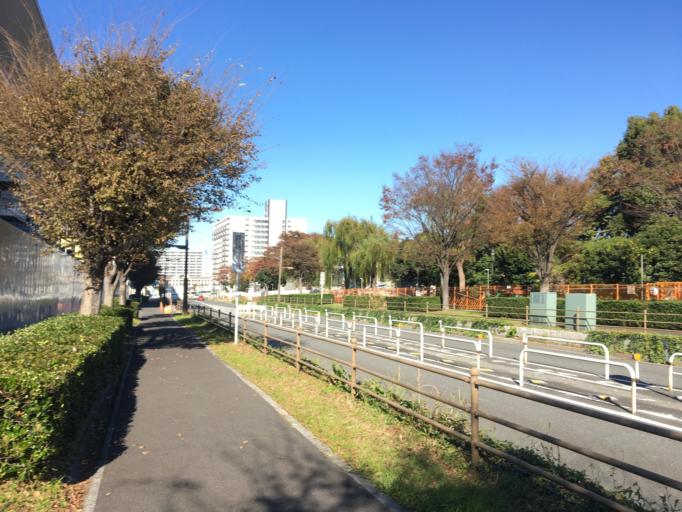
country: JP
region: Tokyo
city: Urayasu
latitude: 35.6505
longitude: 139.8161
